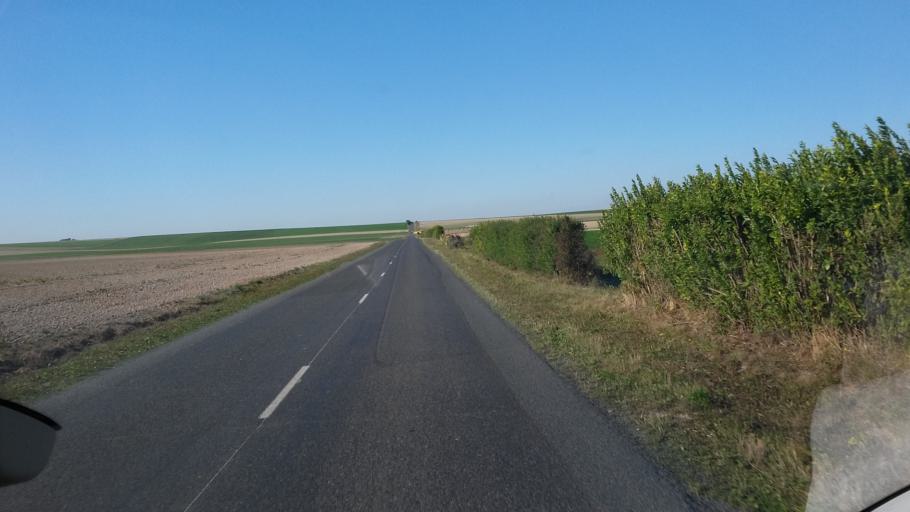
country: FR
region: Champagne-Ardenne
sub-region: Departement de la Marne
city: Connantre
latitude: 48.7529
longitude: 3.8829
